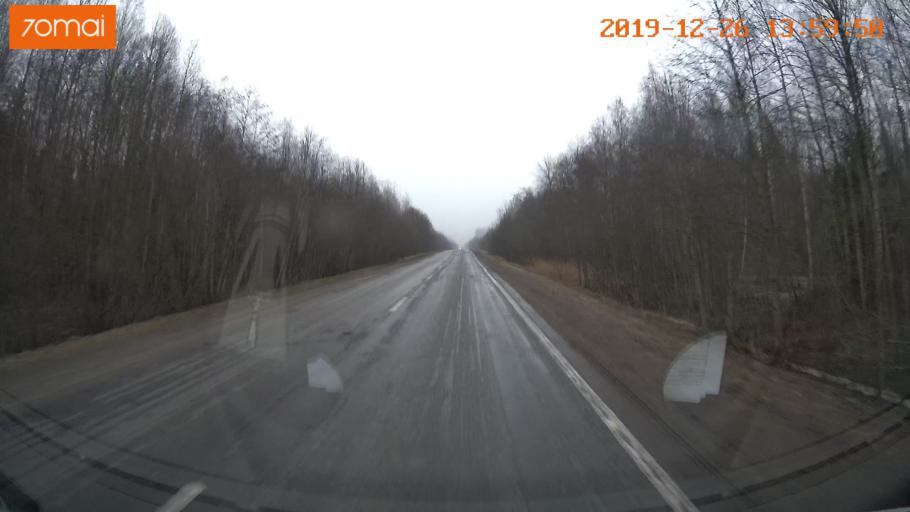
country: RU
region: Jaroslavl
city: Poshekhon'ye
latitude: 58.5625
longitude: 38.7317
